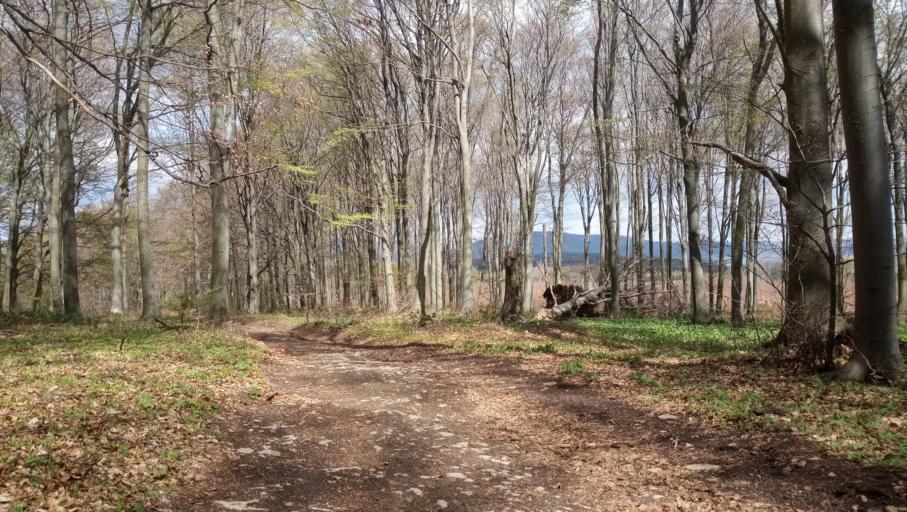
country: HU
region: Veszprem
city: Herend
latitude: 47.2001
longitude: 17.7554
